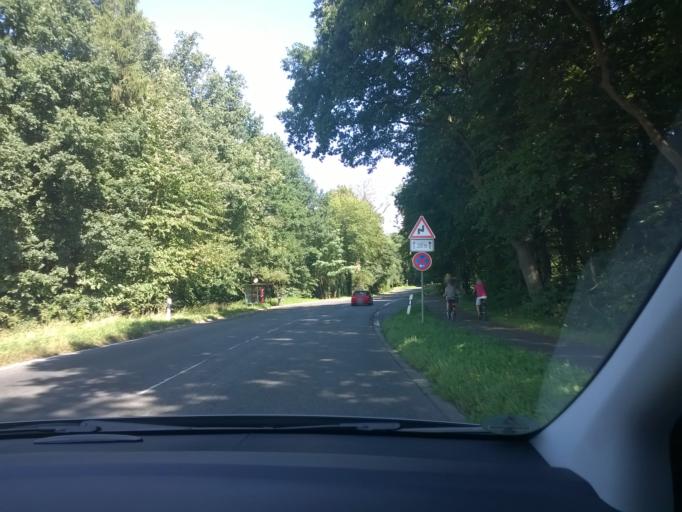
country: DE
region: North Rhine-Westphalia
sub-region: Regierungsbezirk Koln
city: Rath
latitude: 50.9323
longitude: 7.0913
